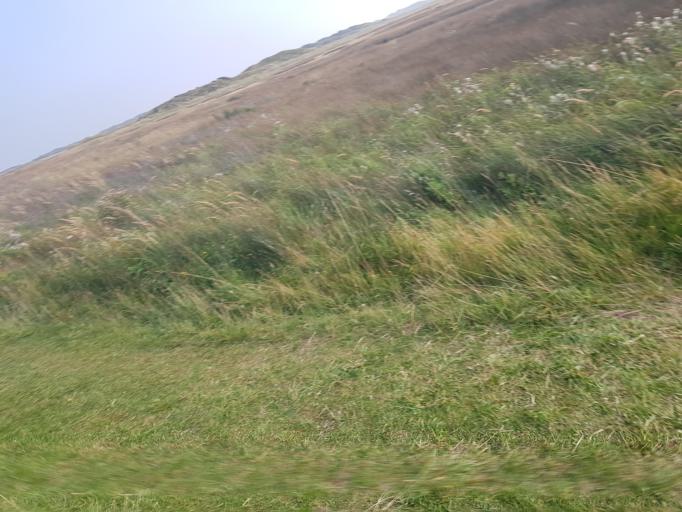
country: NL
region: North Holland
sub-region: Gemeente Texel
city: Den Burg
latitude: 53.1563
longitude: 4.8190
